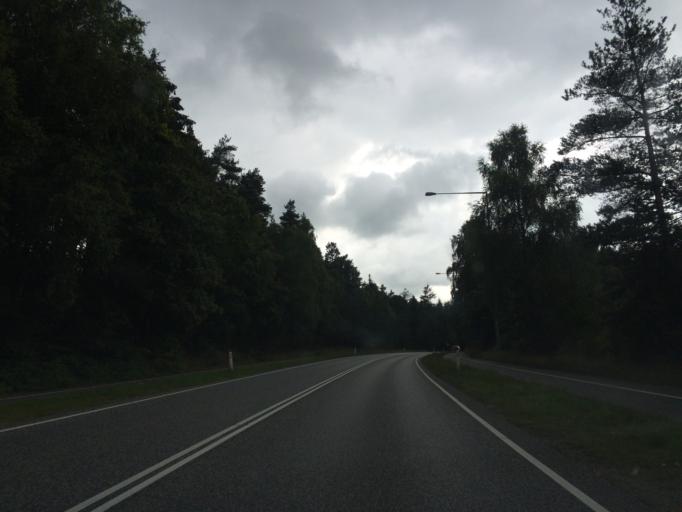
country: DK
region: Central Jutland
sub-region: Silkeborg Kommune
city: Silkeborg
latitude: 56.1655
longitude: 9.5275
